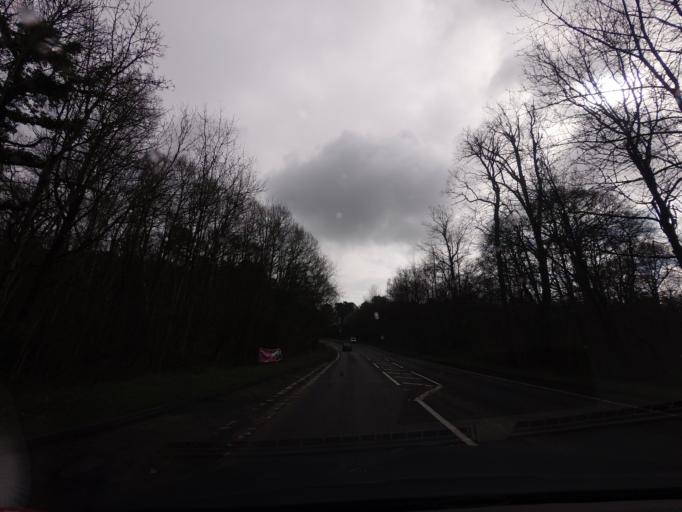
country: GB
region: England
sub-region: Kent
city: Kemsing
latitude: 51.2777
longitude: 0.2628
